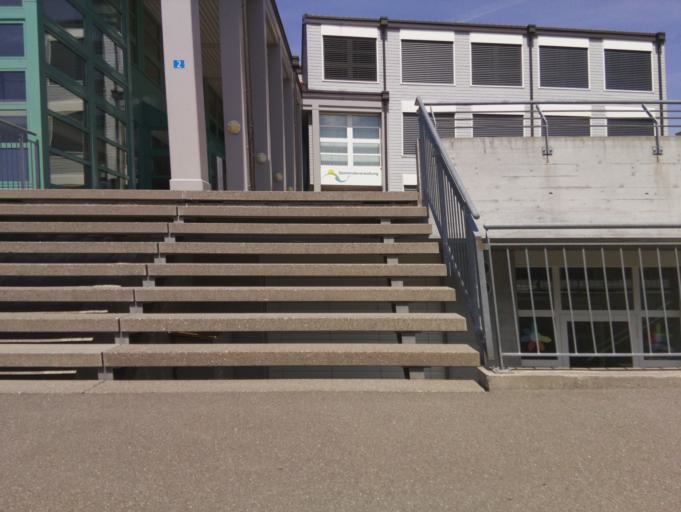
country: CH
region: Schwyz
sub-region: Bezirk March
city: Lachen
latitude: 47.1931
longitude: 8.8944
